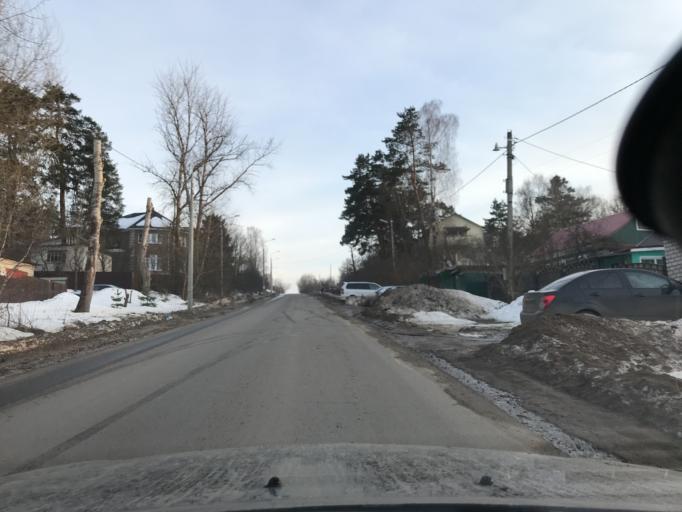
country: RU
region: Kaluga
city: Kaluga
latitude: 54.4974
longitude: 36.2447
